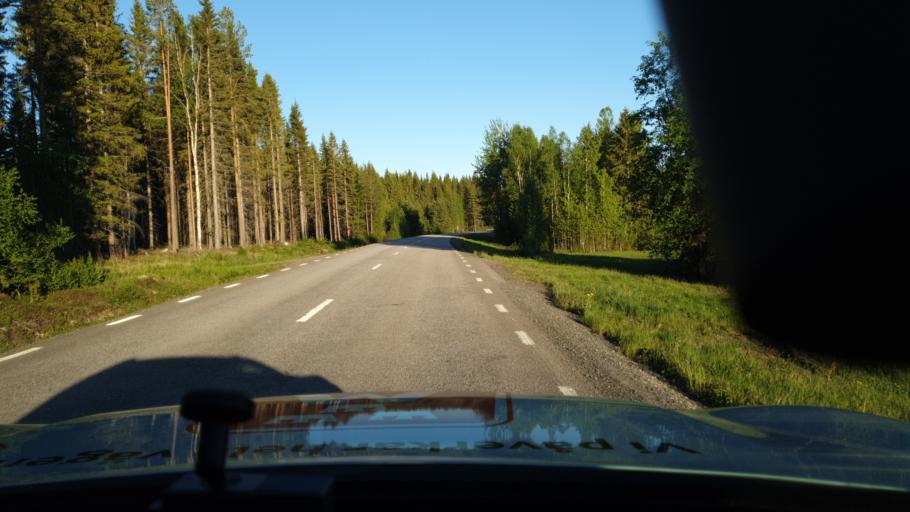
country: SE
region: Vaesterbotten
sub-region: Umea Kommun
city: Ersmark
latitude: 63.9760
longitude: 20.2654
